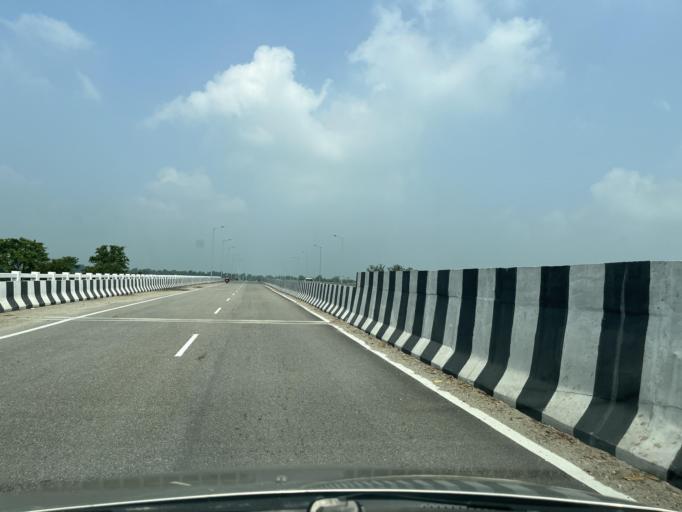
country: IN
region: Uttarakhand
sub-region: Udham Singh Nagar
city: Kashipur
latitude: 29.1733
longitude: 78.9469
